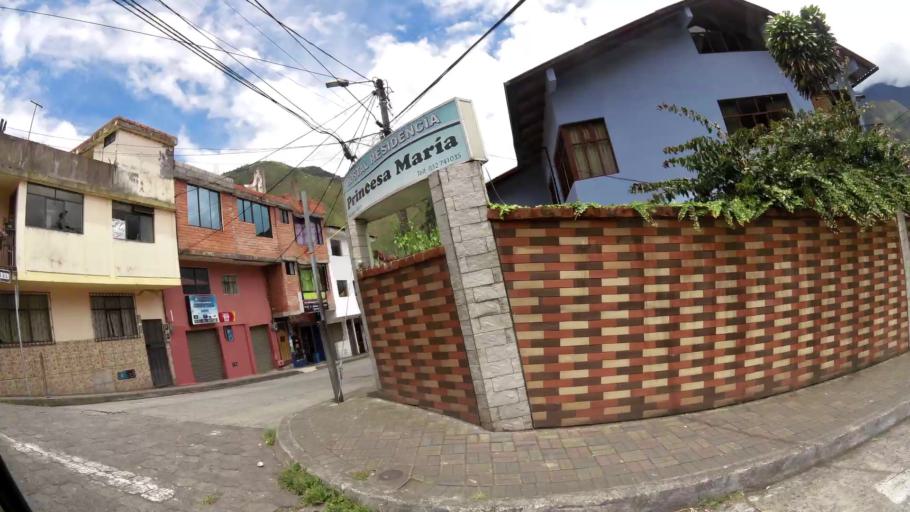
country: EC
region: Tungurahua
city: Banos
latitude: -1.3985
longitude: -78.4261
